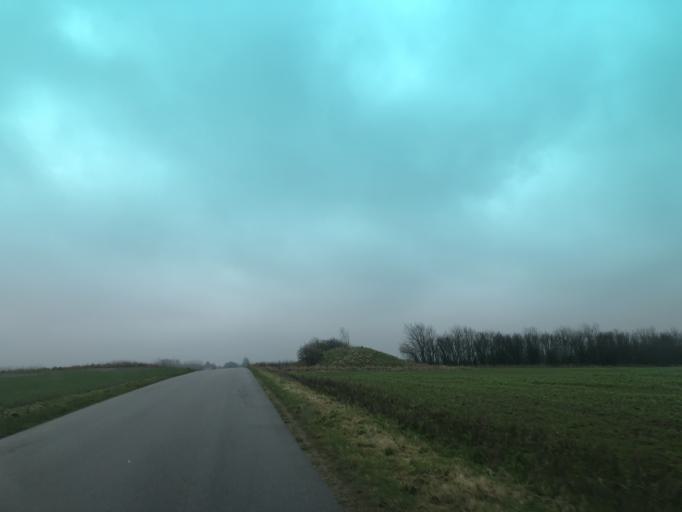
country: DK
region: Central Jutland
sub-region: Struer Kommune
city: Struer
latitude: 56.4451
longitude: 8.5874
